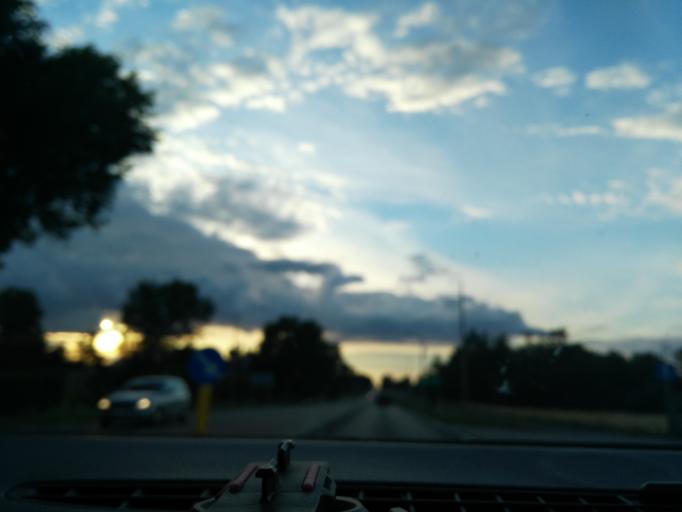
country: PL
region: Lublin Voivodeship
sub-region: Powiat lubartowski
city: Serniki
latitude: 51.4297
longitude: 22.6326
